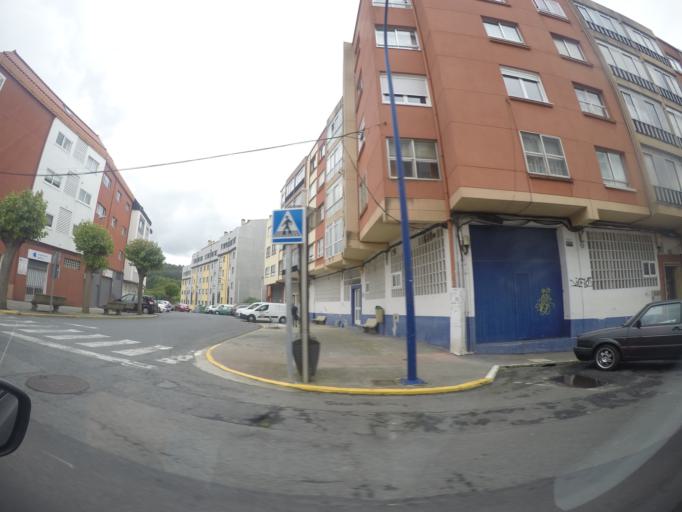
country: ES
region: Galicia
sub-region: Provincia da Coruna
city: Culleredo
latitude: 43.3082
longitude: -8.3831
